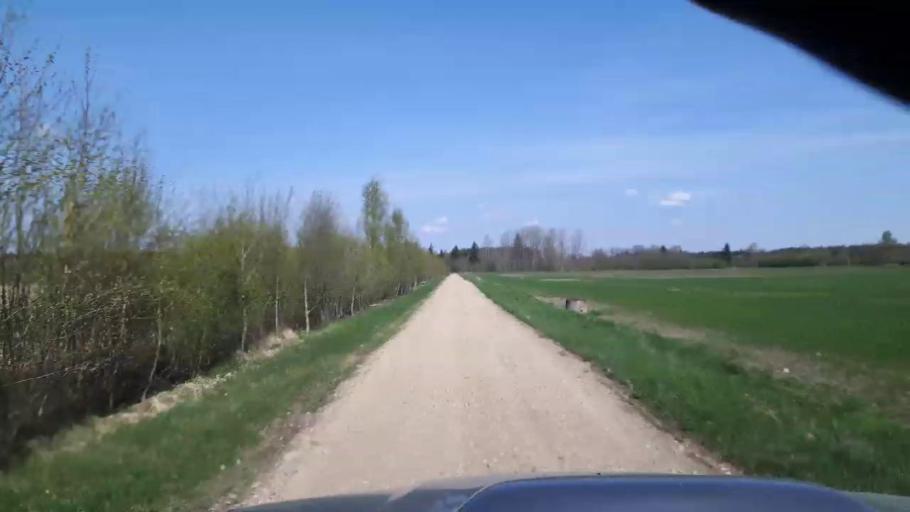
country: EE
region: Paernumaa
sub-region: Tootsi vald
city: Tootsi
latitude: 58.4992
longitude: 24.9408
